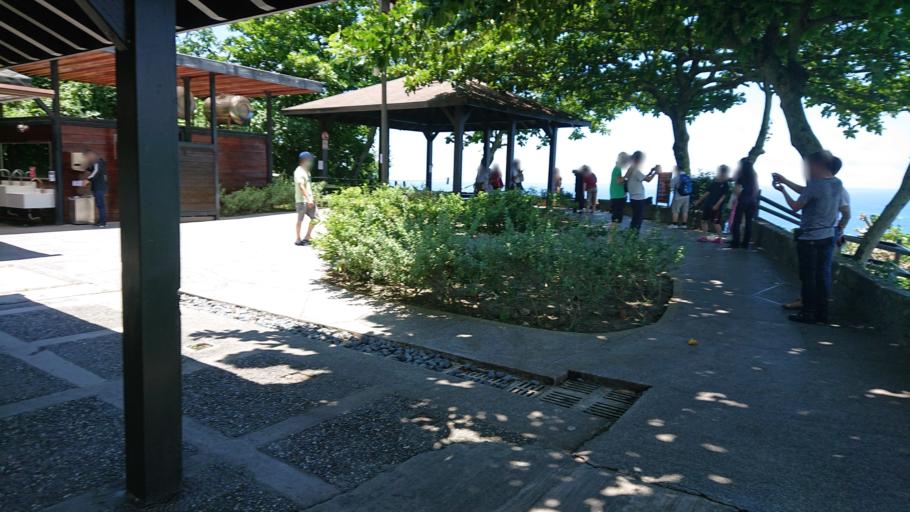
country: TW
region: Taiwan
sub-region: Hualien
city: Hualian
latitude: 23.7312
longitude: 121.5585
